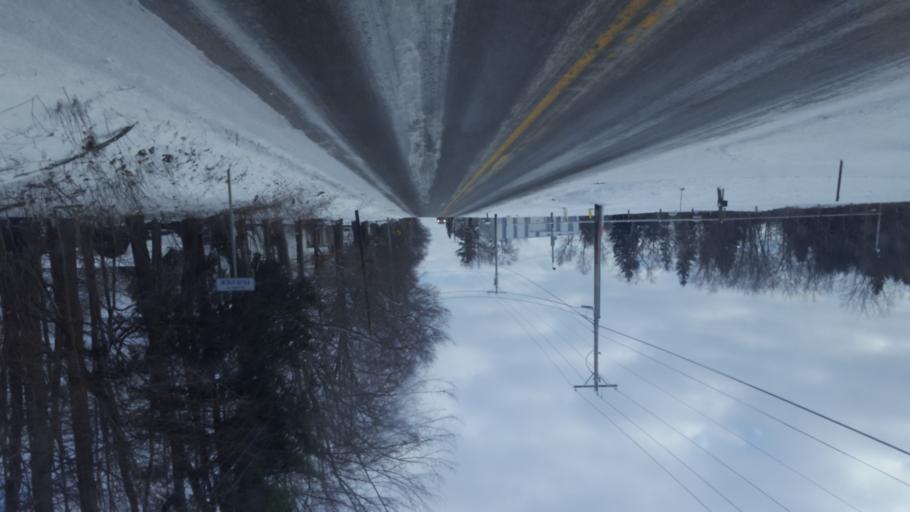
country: US
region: Pennsylvania
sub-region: Mercer County
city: Mercer
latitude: 41.3289
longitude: -80.2296
